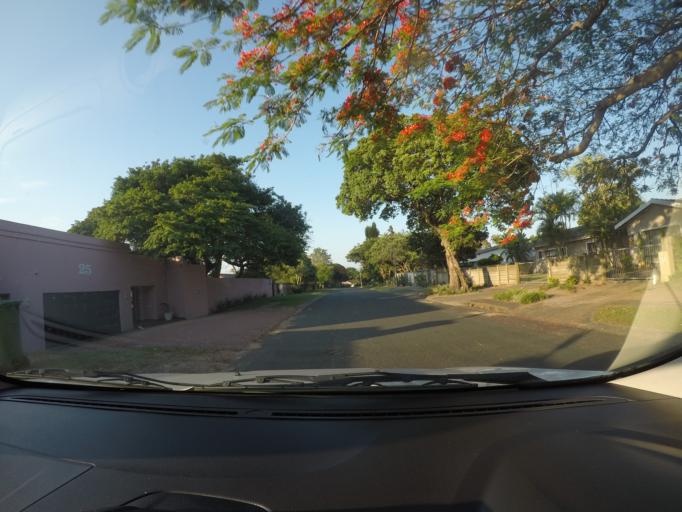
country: ZA
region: KwaZulu-Natal
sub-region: uThungulu District Municipality
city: Richards Bay
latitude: -28.7837
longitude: 32.0917
